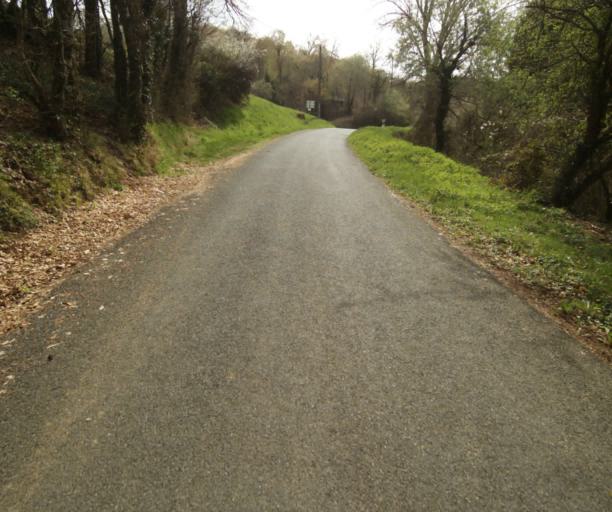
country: FR
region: Limousin
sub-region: Departement de la Correze
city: Naves
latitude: 45.2961
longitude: 1.7758
